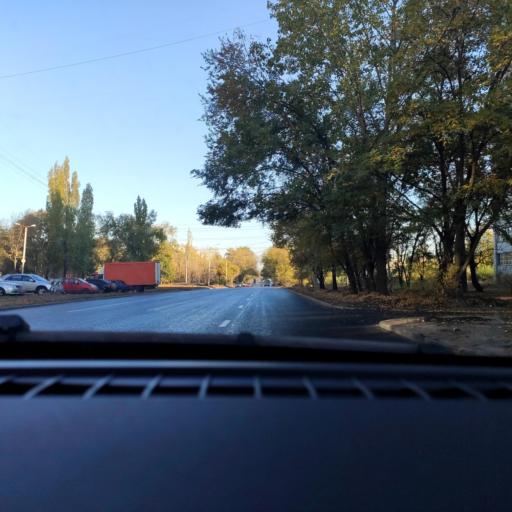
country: RU
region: Voronezj
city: Maslovka
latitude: 51.5971
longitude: 39.2438
